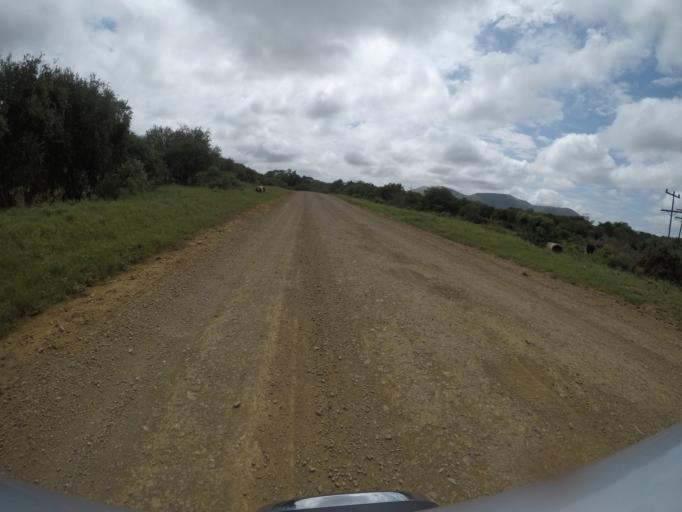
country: ZA
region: KwaZulu-Natal
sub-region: uThungulu District Municipality
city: Empangeni
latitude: -28.5902
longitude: 31.8415
